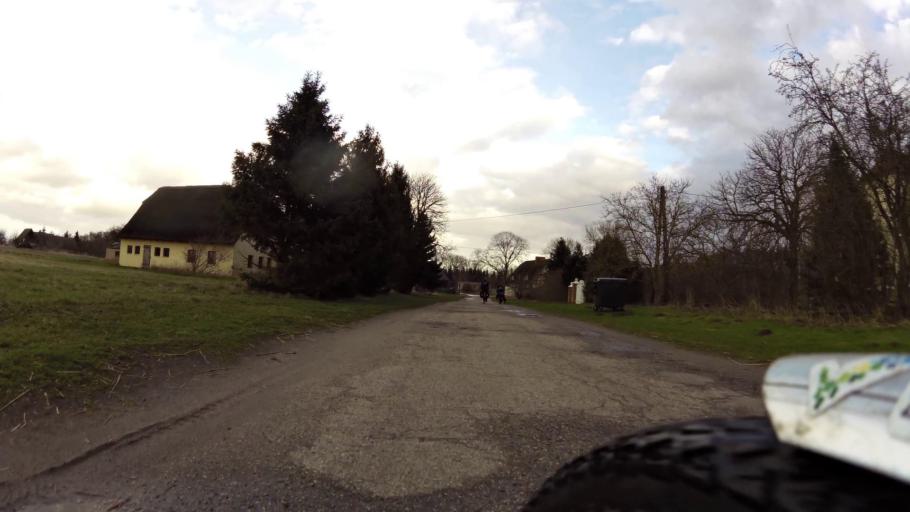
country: PL
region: West Pomeranian Voivodeship
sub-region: Powiat kamienski
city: Kamien Pomorski
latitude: 53.8945
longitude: 14.7252
